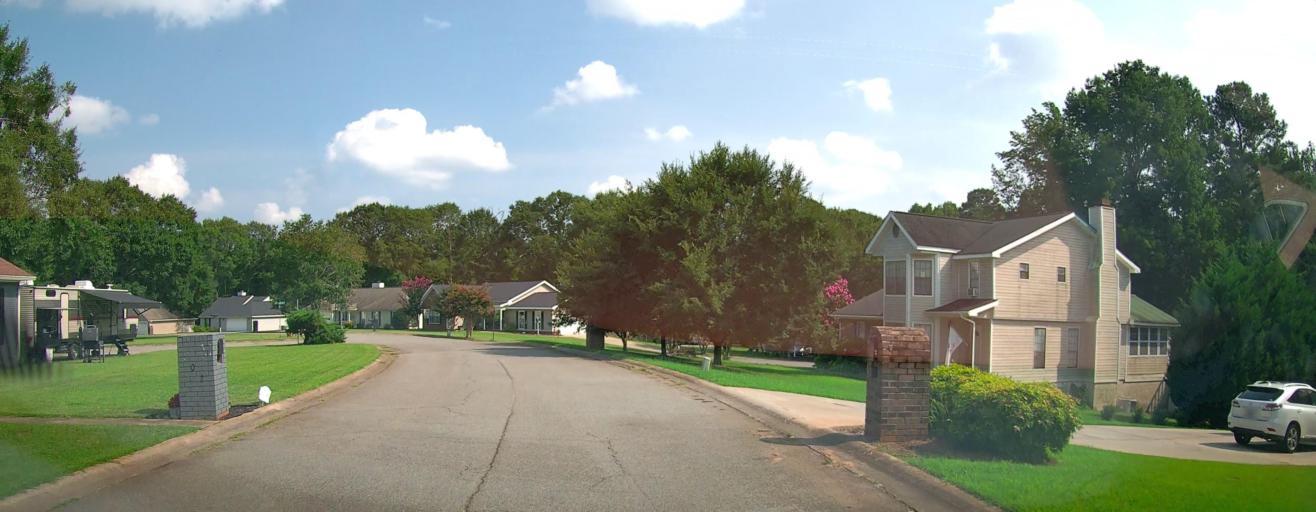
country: US
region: Georgia
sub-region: Houston County
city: Centerville
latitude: 32.6444
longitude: -83.6963
